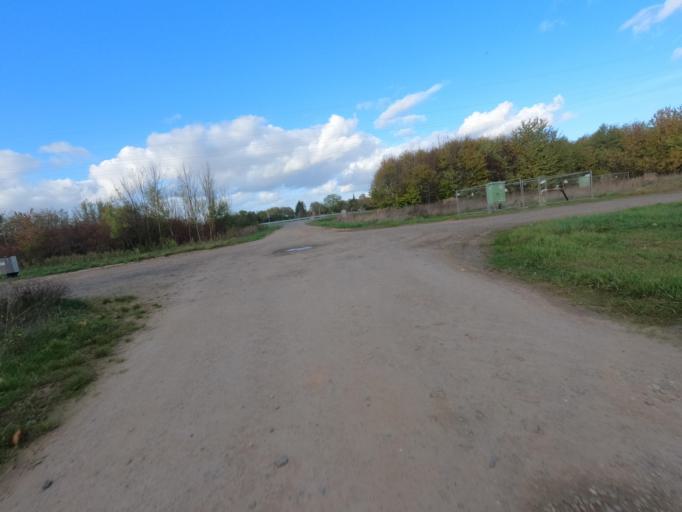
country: DE
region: North Rhine-Westphalia
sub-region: Regierungsbezirk Koln
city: Titz
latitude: 51.0895
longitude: 6.4119
